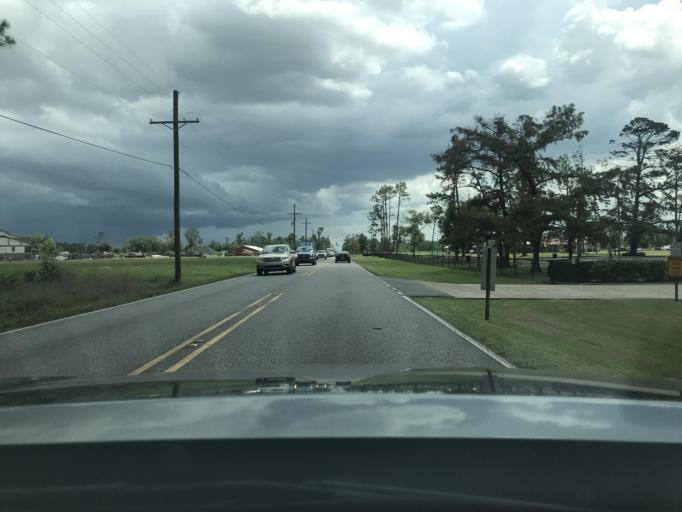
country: US
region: Louisiana
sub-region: Calcasieu Parish
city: Westlake
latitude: 30.2779
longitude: -93.2582
